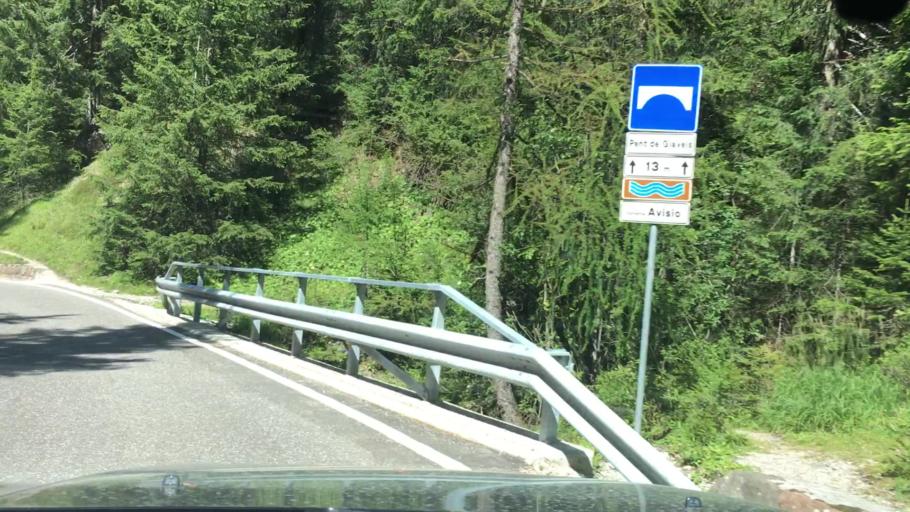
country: IT
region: Trentino-Alto Adige
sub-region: Provincia di Trento
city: Canazei
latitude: 46.4579
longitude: 11.8083
